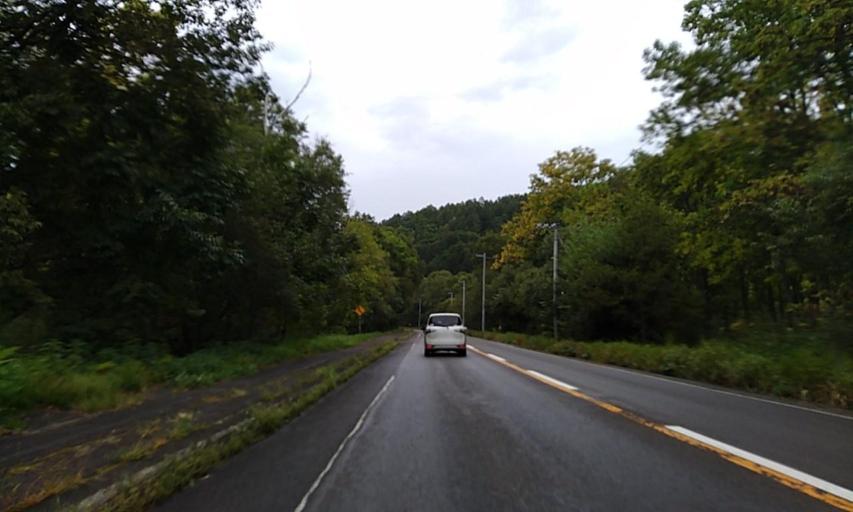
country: JP
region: Hokkaido
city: Abashiri
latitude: 43.9720
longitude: 144.2181
